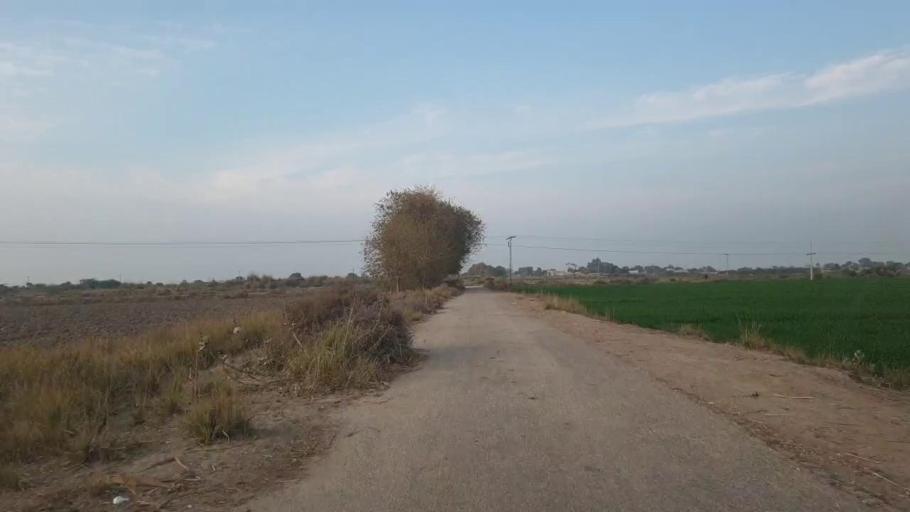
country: PK
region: Sindh
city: Shahpur Chakar
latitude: 26.1171
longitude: 68.5443
